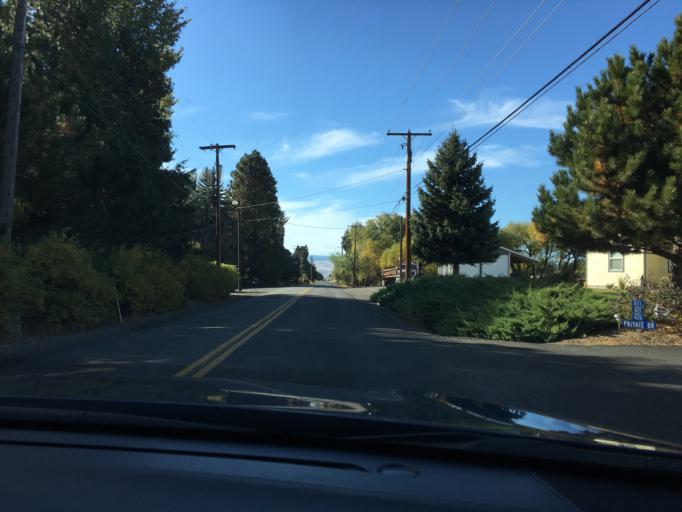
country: US
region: Washington
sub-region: Kittitas County
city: Ellensburg
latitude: 47.0213
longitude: -120.5350
